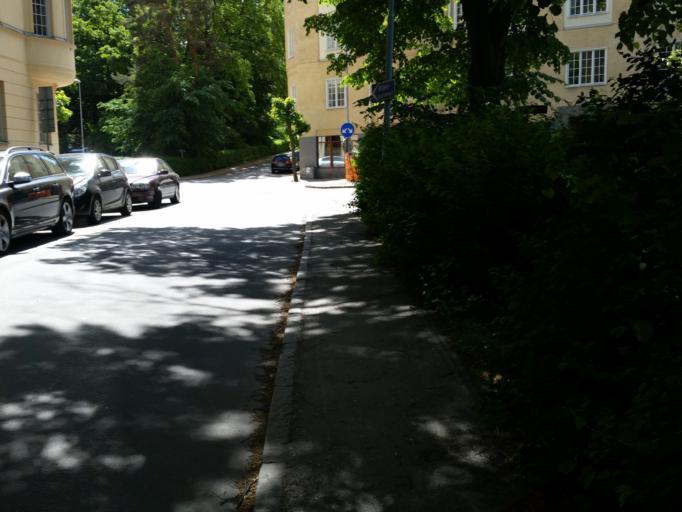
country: SE
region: Stockholm
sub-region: Solna Kommun
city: Rasunda
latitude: 59.3666
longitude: 17.9932
